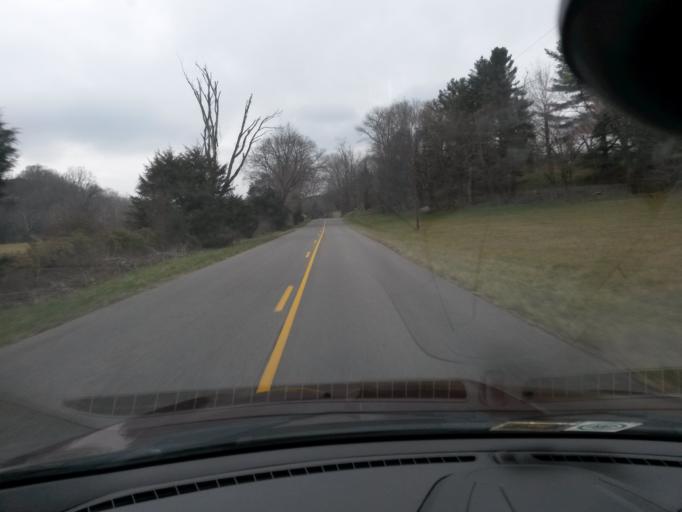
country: US
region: Virginia
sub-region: City of Lexington
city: Lexington
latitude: 37.8554
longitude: -79.4974
